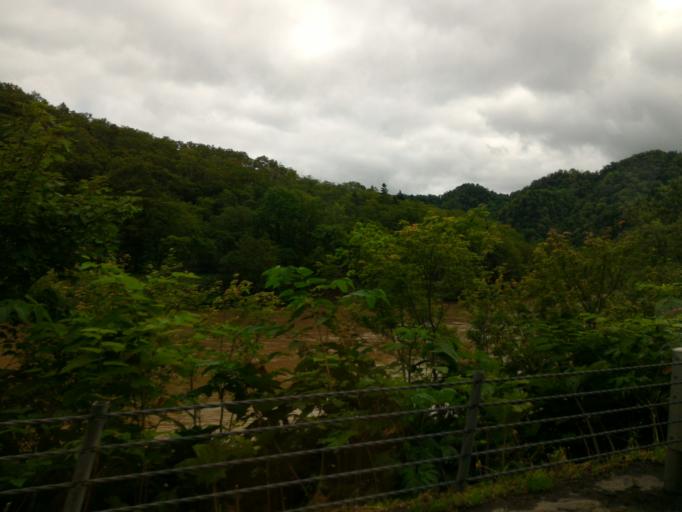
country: JP
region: Hokkaido
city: Nayoro
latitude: 44.7254
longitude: 142.1665
